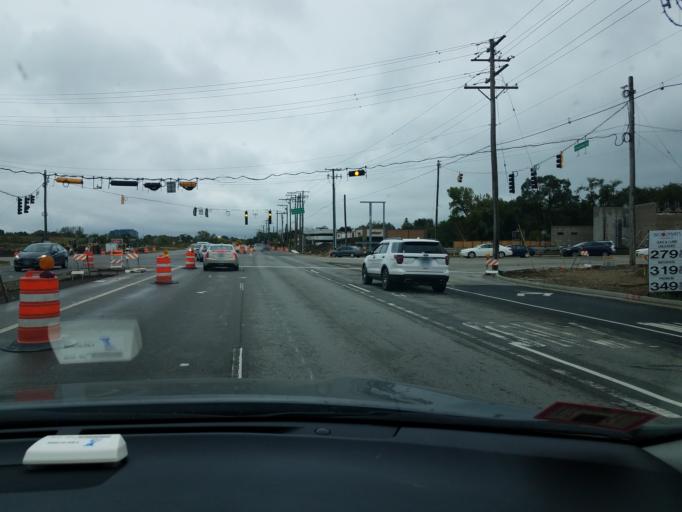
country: US
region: Illinois
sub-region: Lake County
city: Riverwoods
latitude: 42.1681
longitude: -87.9220
